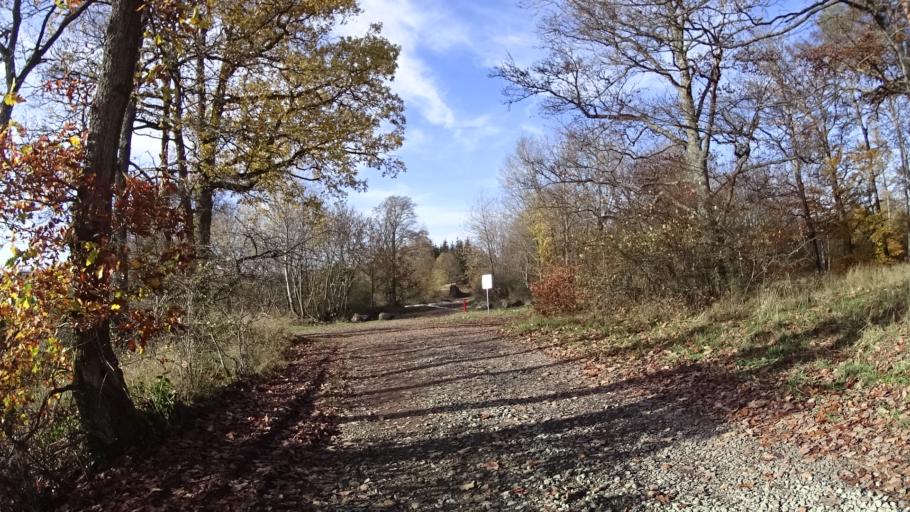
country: DE
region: Rheinland-Pfalz
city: Unterjeckenbach
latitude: 49.6503
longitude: 7.4886
